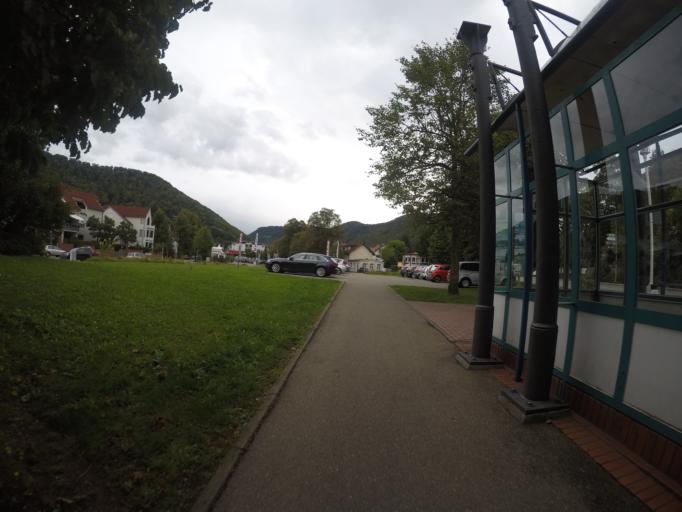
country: DE
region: Baden-Wuerttemberg
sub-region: Tuebingen Region
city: Pfullingen
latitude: 48.4305
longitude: 9.2549
